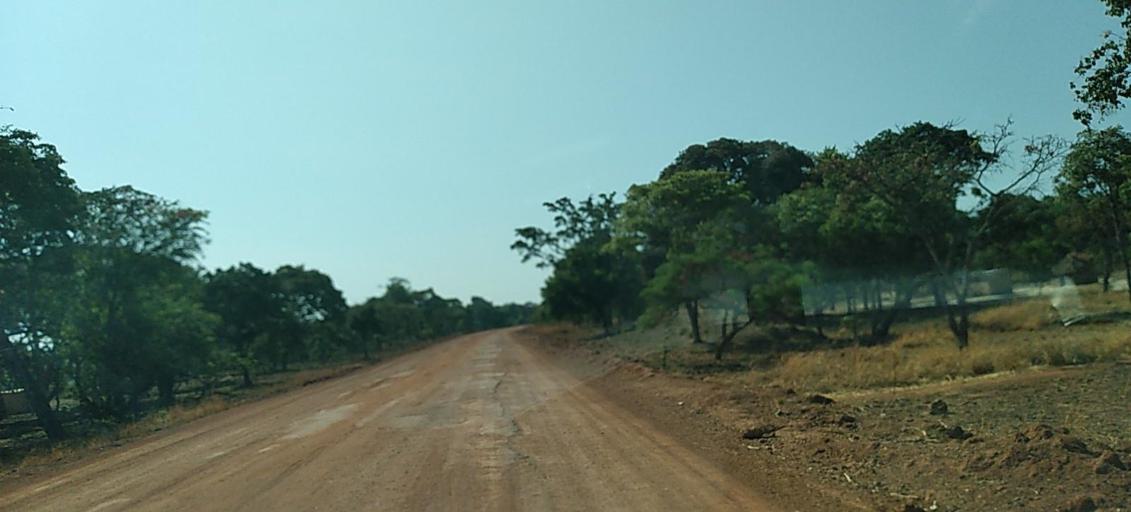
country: ZM
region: North-Western
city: Mwinilunga
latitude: -11.9195
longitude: 25.3144
